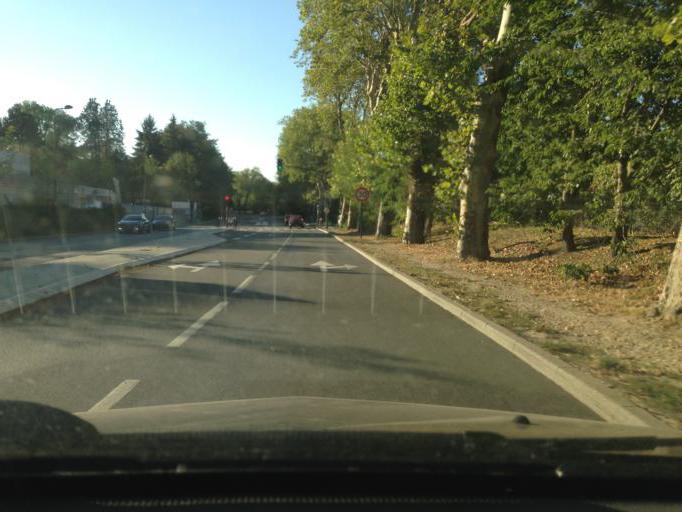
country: FR
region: Ile-de-France
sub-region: Departement des Yvelines
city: Louveciennes
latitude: 48.8700
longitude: 2.1124
